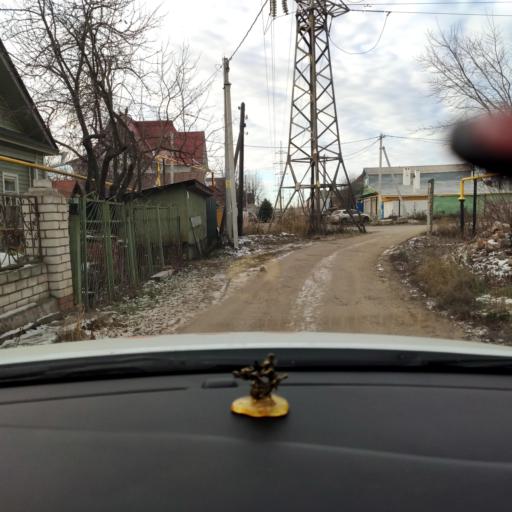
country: RU
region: Tatarstan
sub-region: Gorod Kazan'
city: Kazan
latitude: 55.7254
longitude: 49.1347
